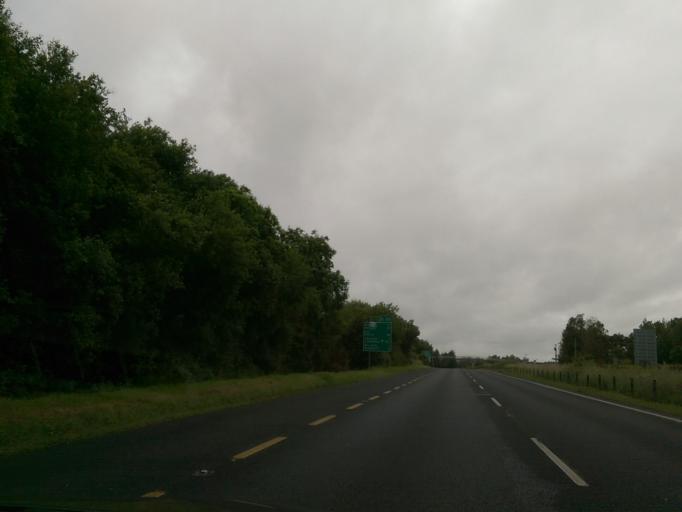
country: IE
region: Munster
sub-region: An Clar
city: Sixmilebridge
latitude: 52.6924
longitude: -8.7541
